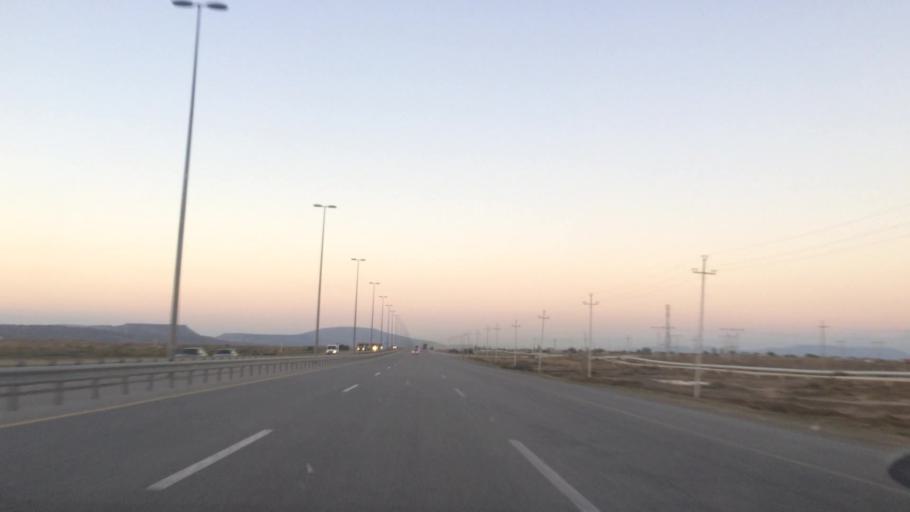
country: AZ
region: Baki
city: Qobustan
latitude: 40.0033
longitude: 49.4292
